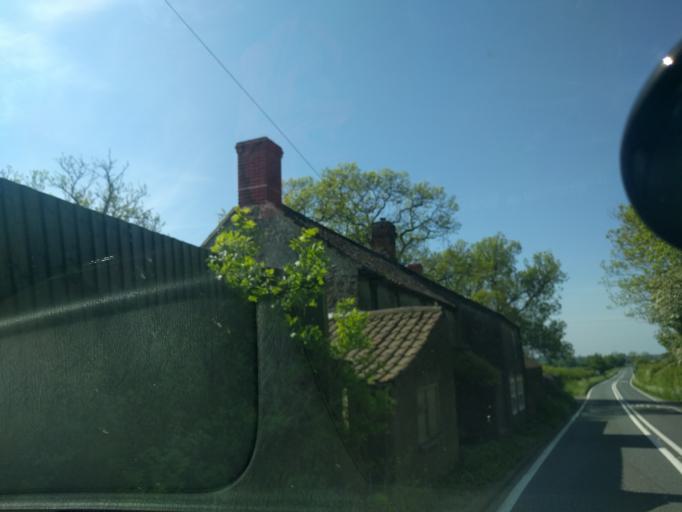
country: GB
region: England
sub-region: Somerset
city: Castle Cary
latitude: 51.1244
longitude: -2.5726
